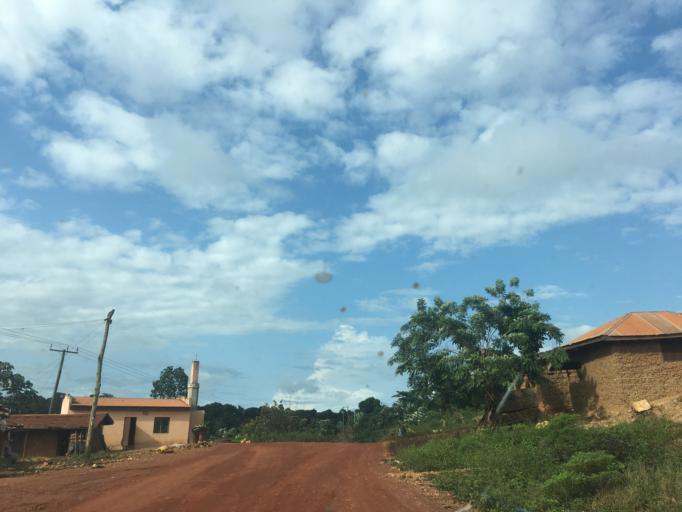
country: GH
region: Western
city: Wassa-Akropong
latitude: 5.9591
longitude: -2.4301
